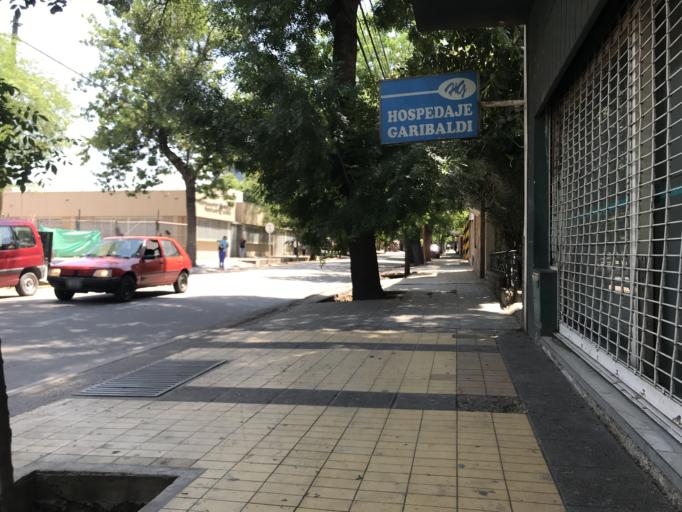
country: AR
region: Mendoza
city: Mendoza
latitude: -32.8912
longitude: -68.8332
